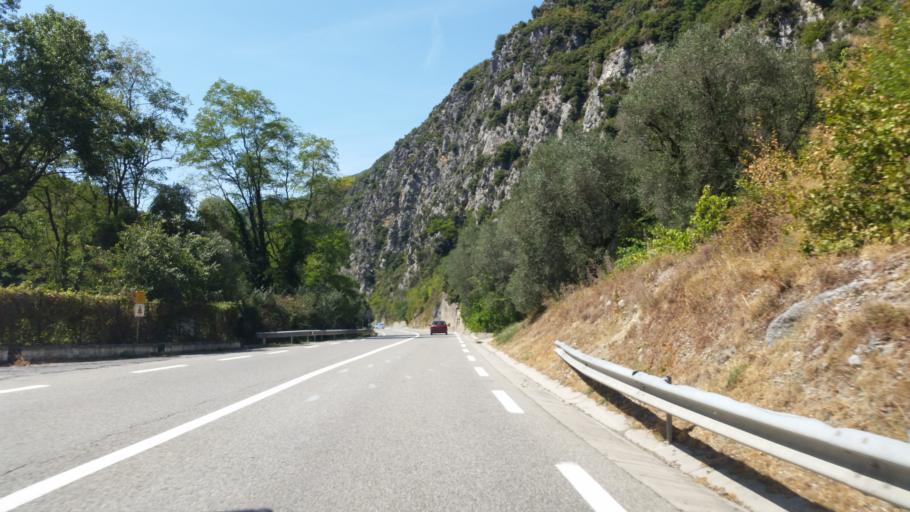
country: FR
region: Provence-Alpes-Cote d'Azur
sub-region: Departement des Alpes-Maritimes
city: Breil-sur-Roya
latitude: 43.9681
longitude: 7.5299
